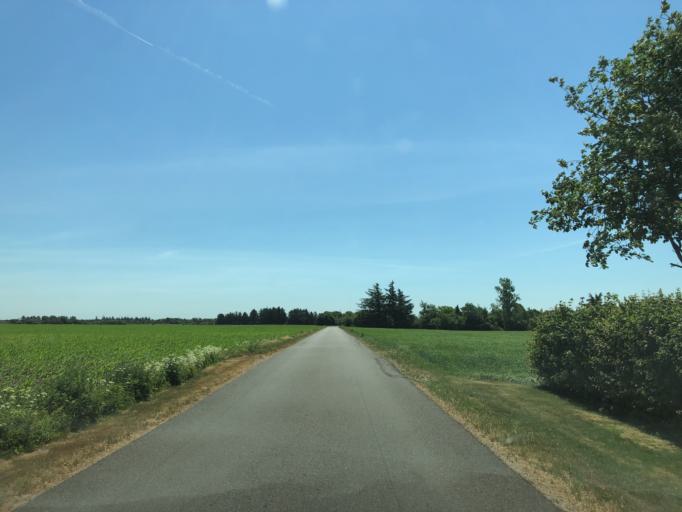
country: DK
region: Central Jutland
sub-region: Holstebro Kommune
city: Ulfborg
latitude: 56.3948
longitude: 8.4277
